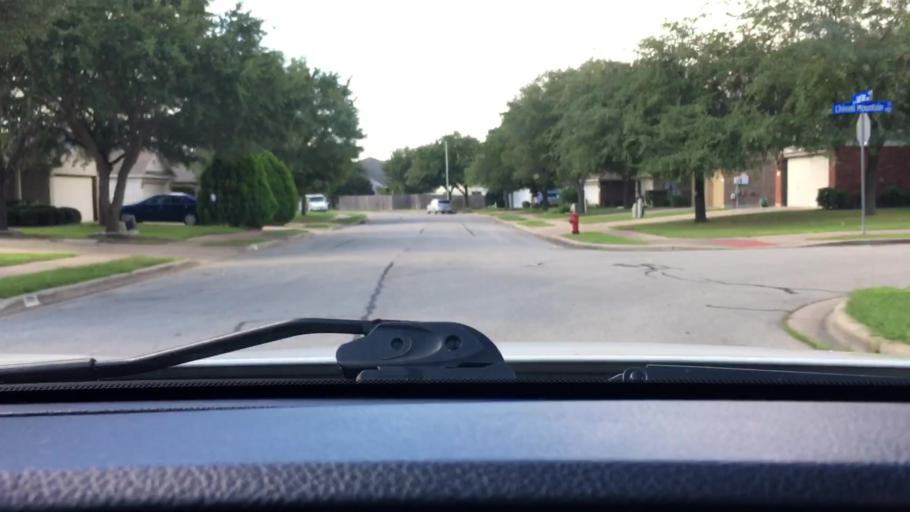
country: US
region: Texas
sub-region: Travis County
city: Windemere
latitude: 30.4738
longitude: -97.6486
